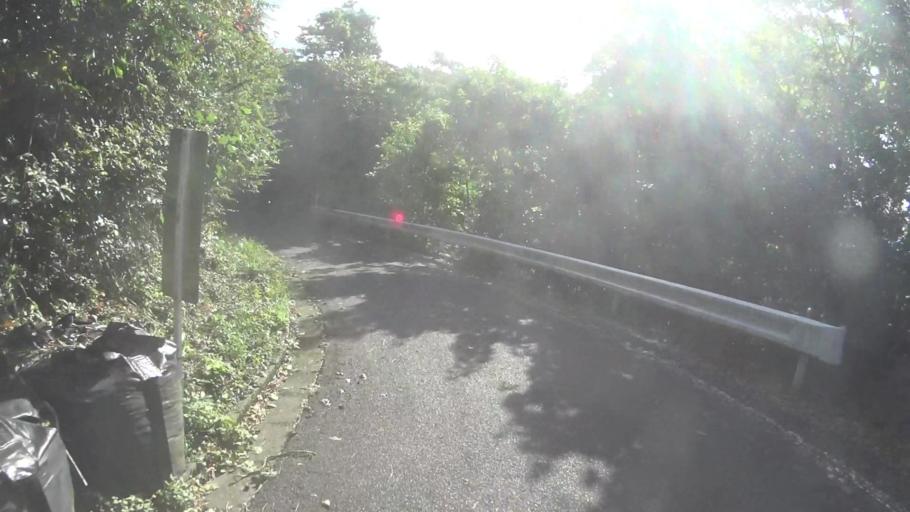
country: JP
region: Kyoto
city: Maizuru
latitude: 35.5657
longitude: 135.4103
